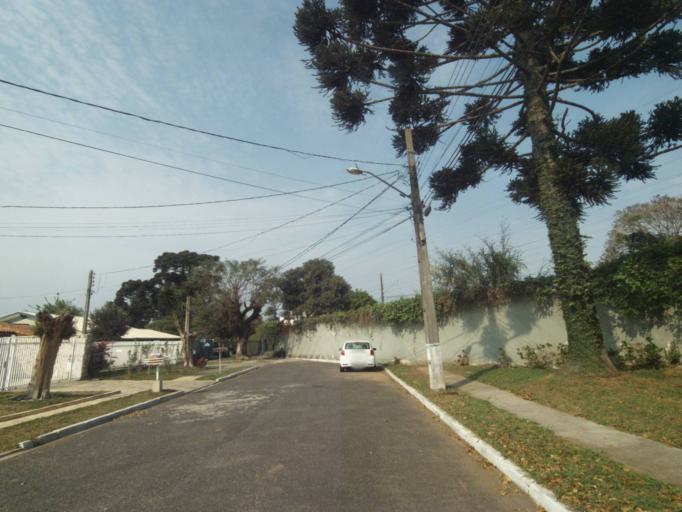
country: BR
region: Parana
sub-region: Pinhais
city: Pinhais
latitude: -25.4848
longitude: -49.2072
